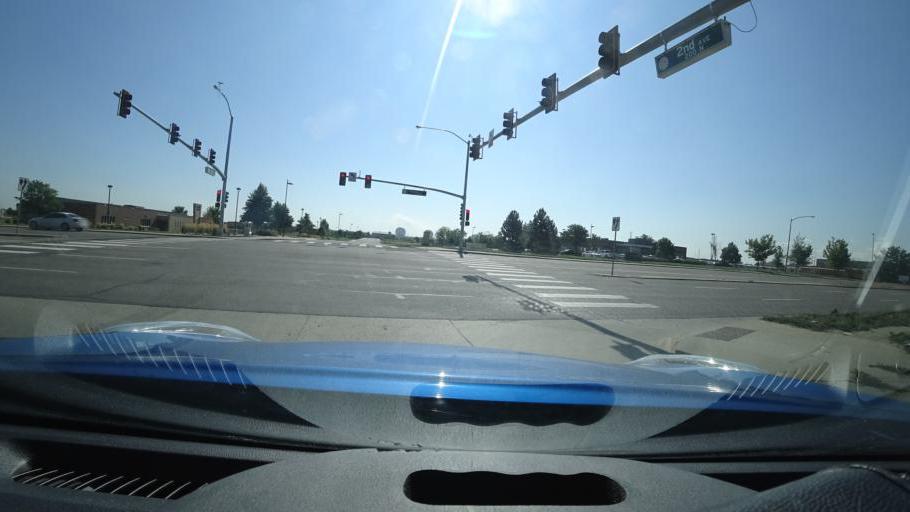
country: US
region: Colorado
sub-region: Adams County
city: Aurora
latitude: 39.7194
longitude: -104.7913
